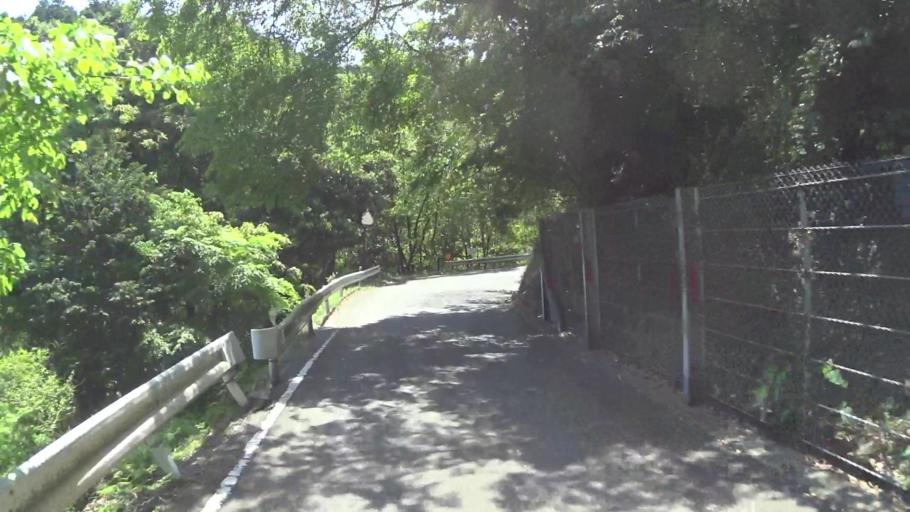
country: JP
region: Kyoto
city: Kameoka
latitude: 35.1332
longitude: 135.5845
